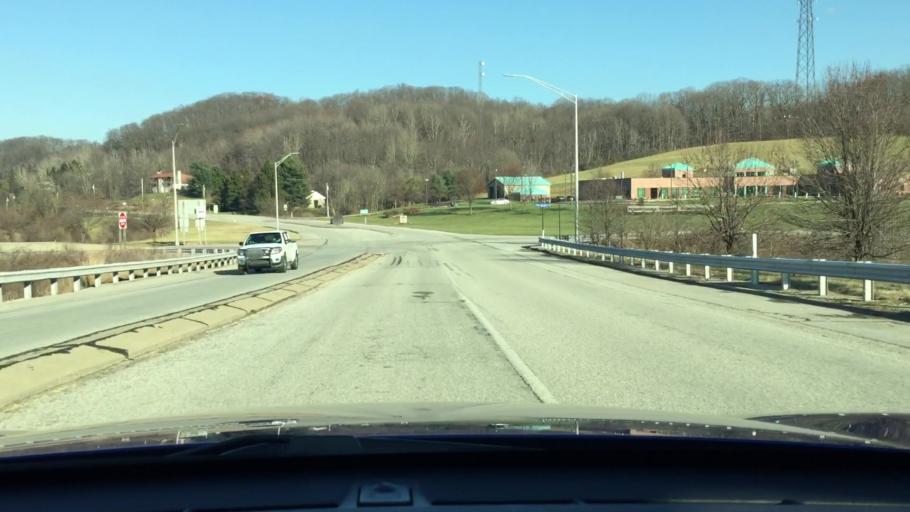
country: US
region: Pennsylvania
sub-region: Westmoreland County
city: New Stanton
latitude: 40.2331
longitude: -79.6000
